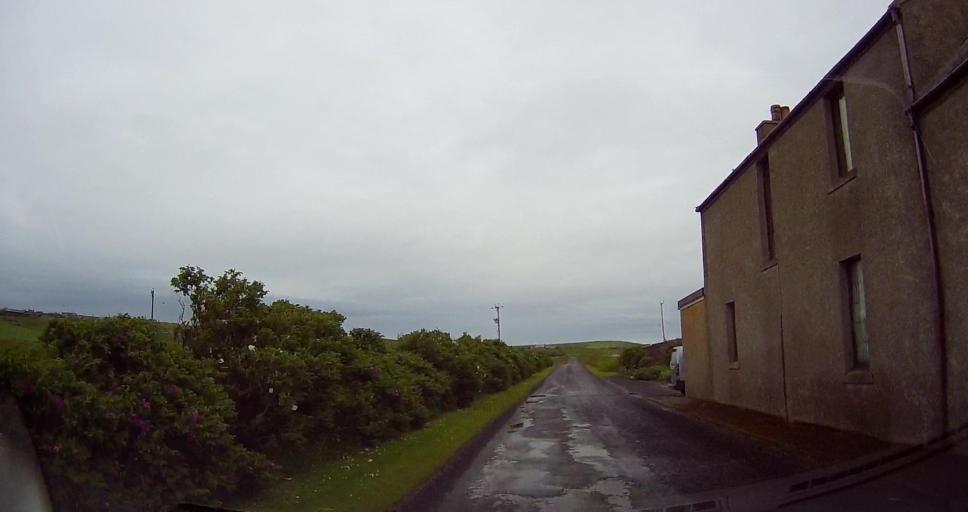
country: GB
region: Scotland
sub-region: Orkney Islands
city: Stromness
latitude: 59.1271
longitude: -3.2938
